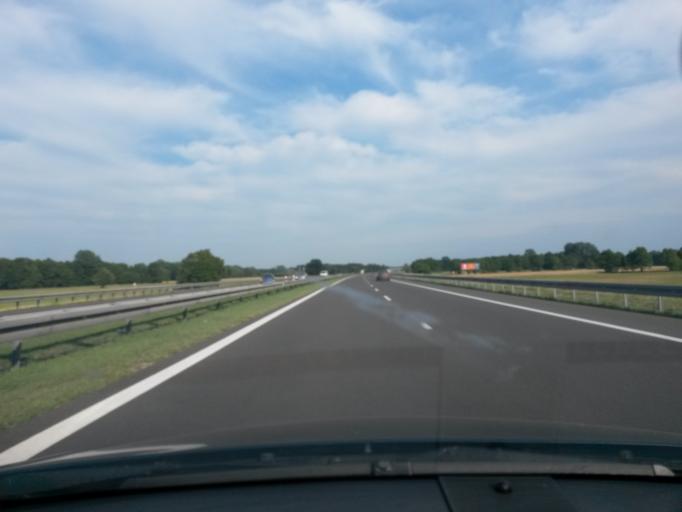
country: PL
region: Greater Poland Voivodeship
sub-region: Powiat koninski
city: Rzgow Pierwszy
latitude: 52.1924
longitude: 18.0675
